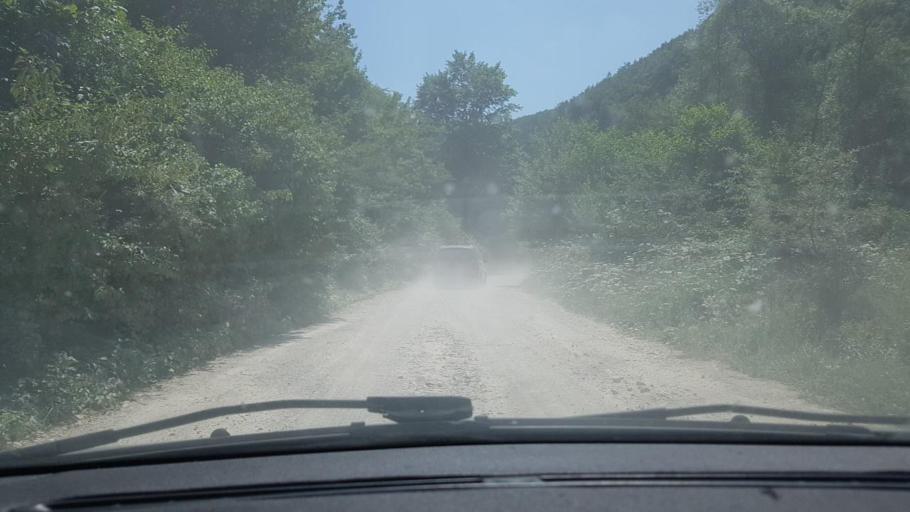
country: BA
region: Federation of Bosnia and Herzegovina
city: Orasac
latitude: 44.6501
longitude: 16.0324
